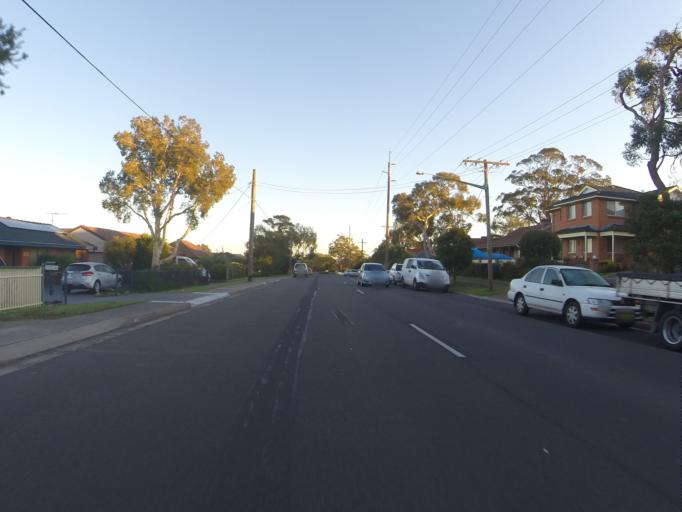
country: AU
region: New South Wales
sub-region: Sutherland Shire
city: Engadine
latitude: -34.0705
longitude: 151.0080
